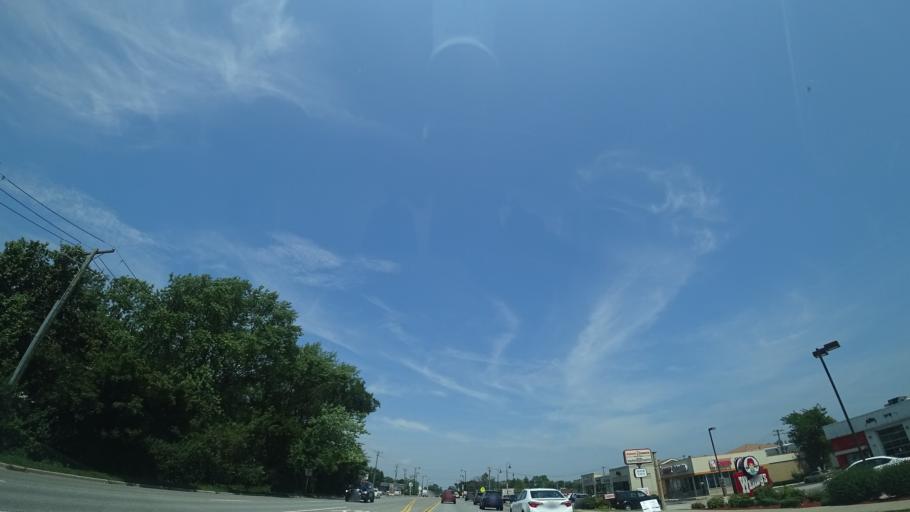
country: US
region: Illinois
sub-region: Cook County
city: Palos Heights
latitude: 41.6582
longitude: -87.7961
